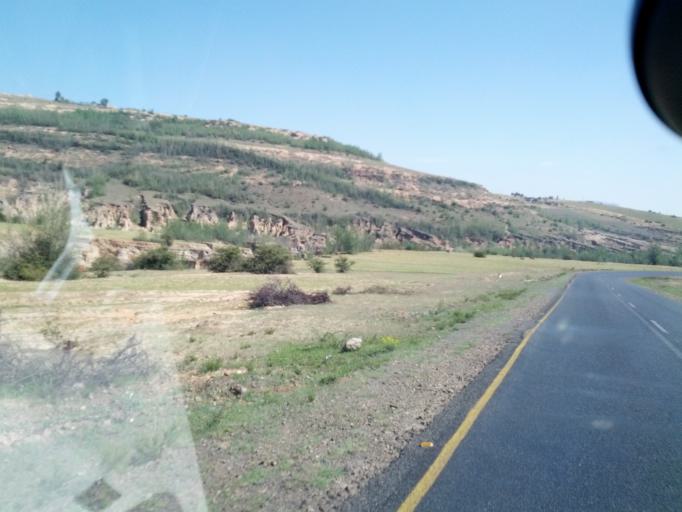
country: LS
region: Berea
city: Teyateyaneng
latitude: -29.1406
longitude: 27.7039
